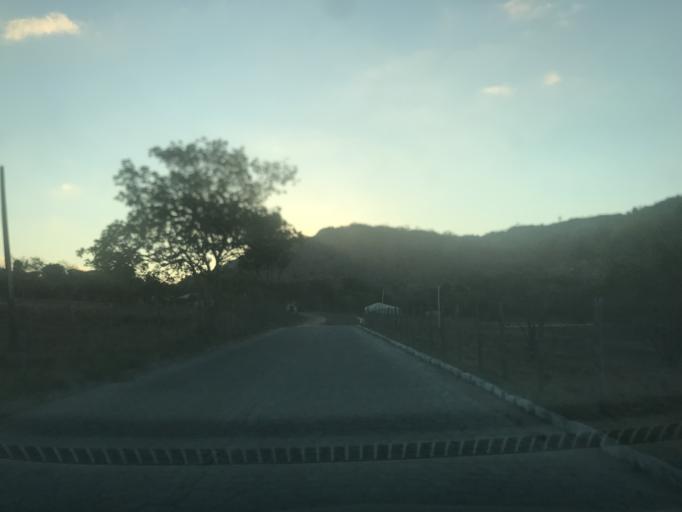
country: BR
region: Pernambuco
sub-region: Bezerros
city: Bezerros
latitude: -8.1905
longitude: -35.7599
